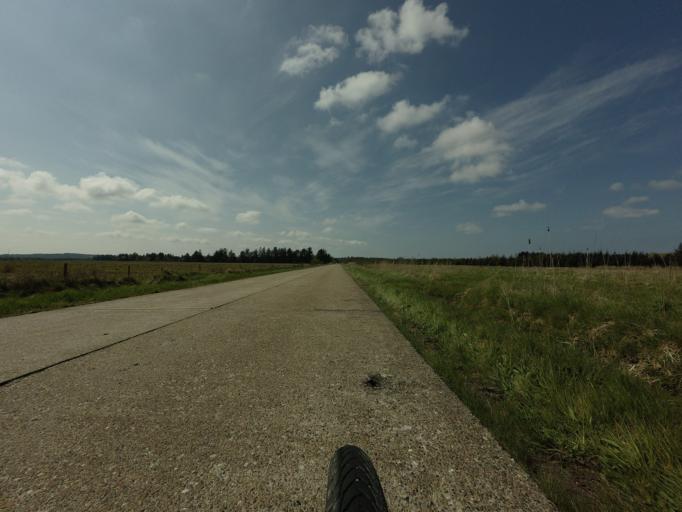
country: DK
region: North Denmark
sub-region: Jammerbugt Kommune
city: Brovst
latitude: 57.1644
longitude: 9.4991
